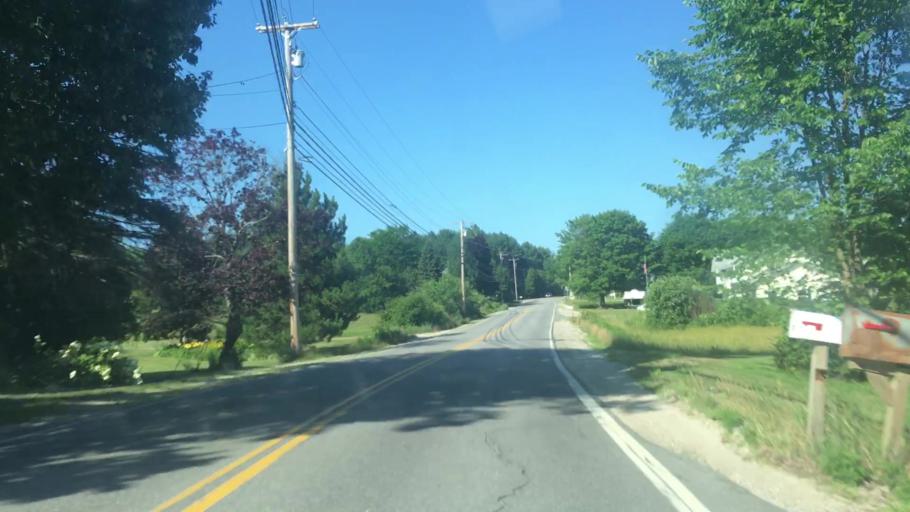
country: US
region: Maine
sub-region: York County
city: Hollis Center
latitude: 43.6767
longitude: -70.5921
